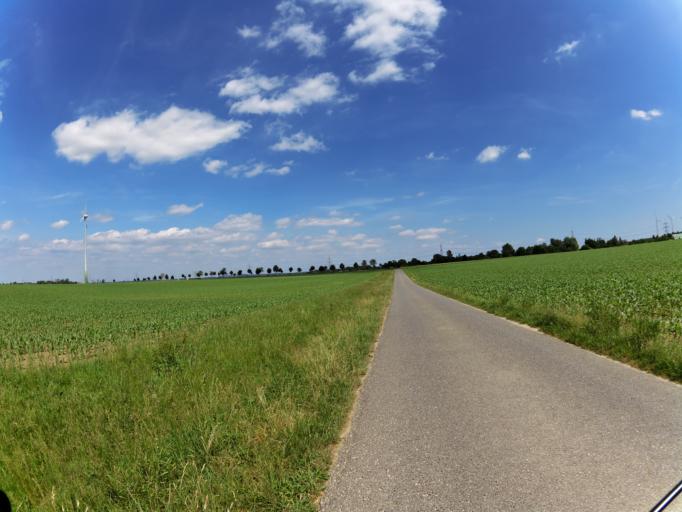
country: DE
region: North Rhine-Westphalia
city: Geilenkirchen
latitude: 51.0151
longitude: 6.1092
